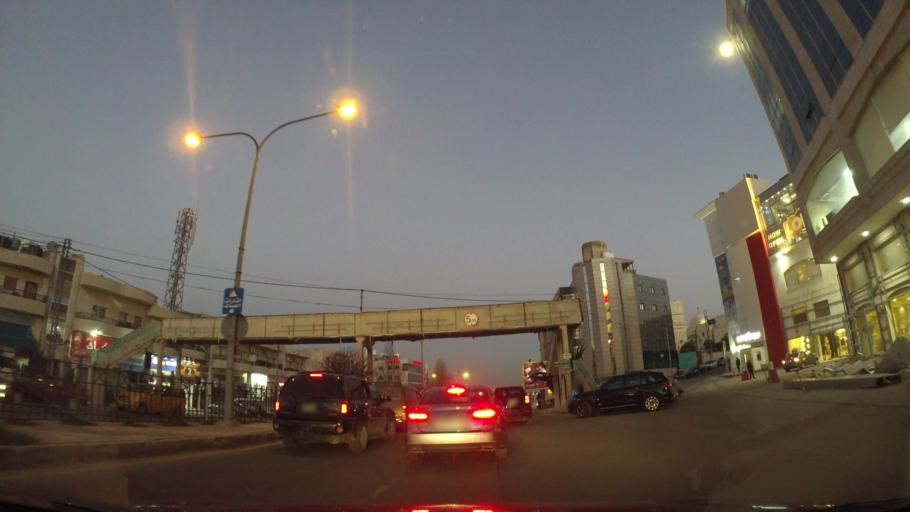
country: JO
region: Amman
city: Al Jubayhah
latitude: 31.9967
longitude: 35.8535
